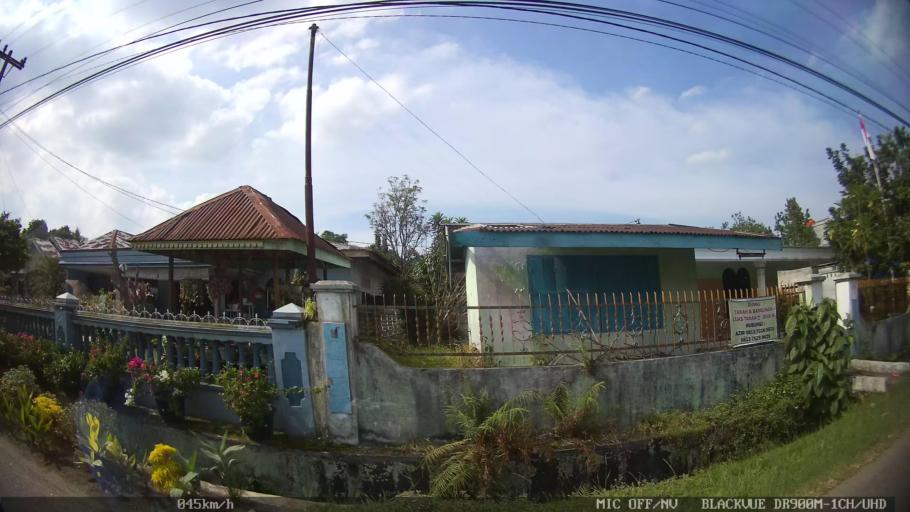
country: ID
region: North Sumatra
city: Binjai
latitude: 3.6438
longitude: 98.5123
